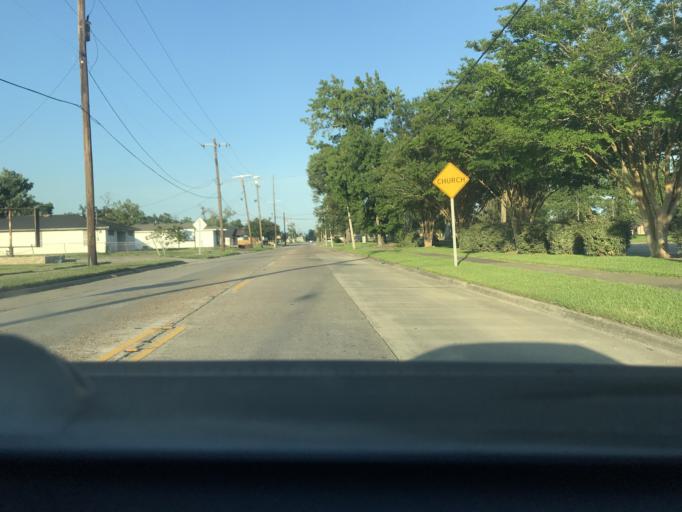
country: US
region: Louisiana
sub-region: Calcasieu Parish
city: Lake Charles
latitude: 30.2496
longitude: -93.1966
